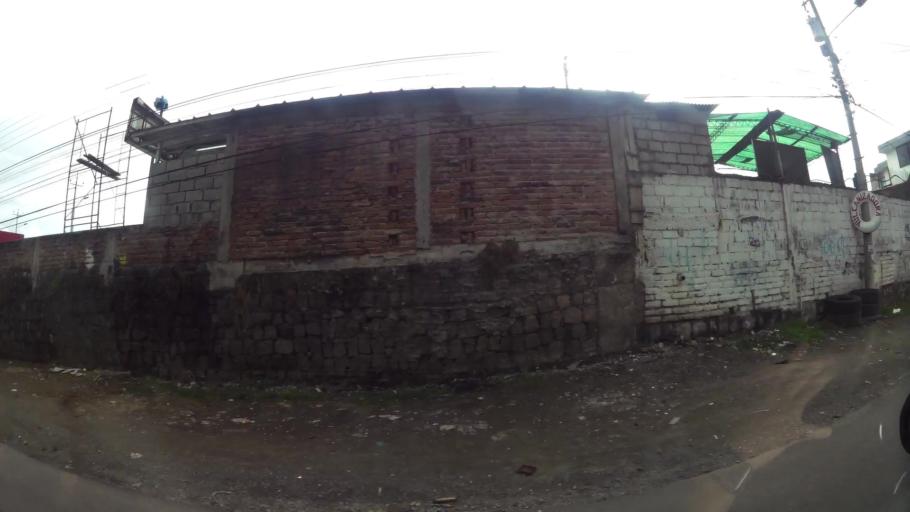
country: EC
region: Pichincha
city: Machachi
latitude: -0.4079
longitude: -78.5467
